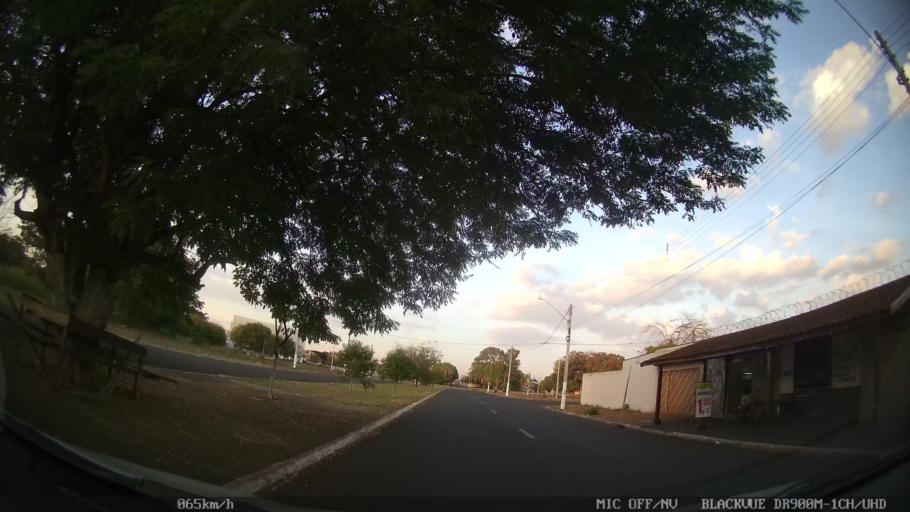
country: BR
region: Sao Paulo
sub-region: Ribeirao Preto
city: Ribeirao Preto
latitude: -21.1269
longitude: -47.8313
